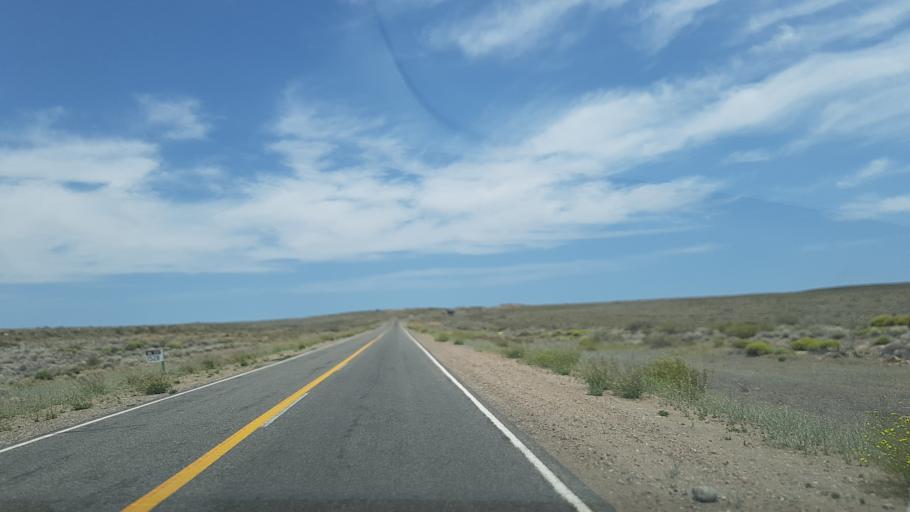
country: AR
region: Rio Negro
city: Pilcaniyeu
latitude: -40.4973
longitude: -70.6785
